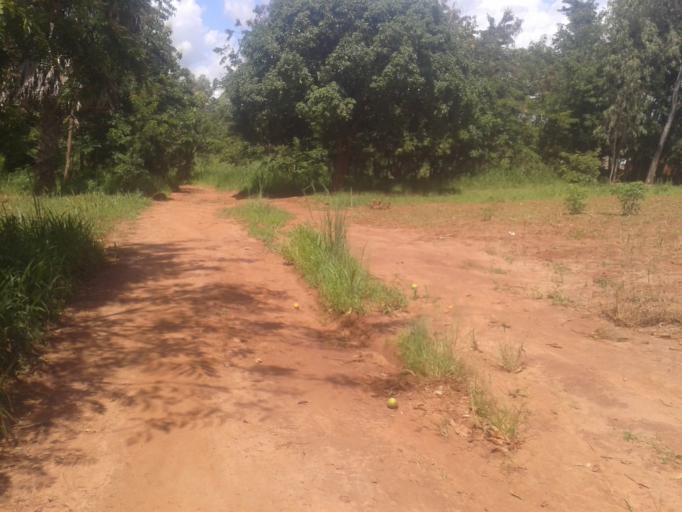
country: UG
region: Northern Region
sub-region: Gulu District
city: Gulu
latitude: 2.7701
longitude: 32.3281
